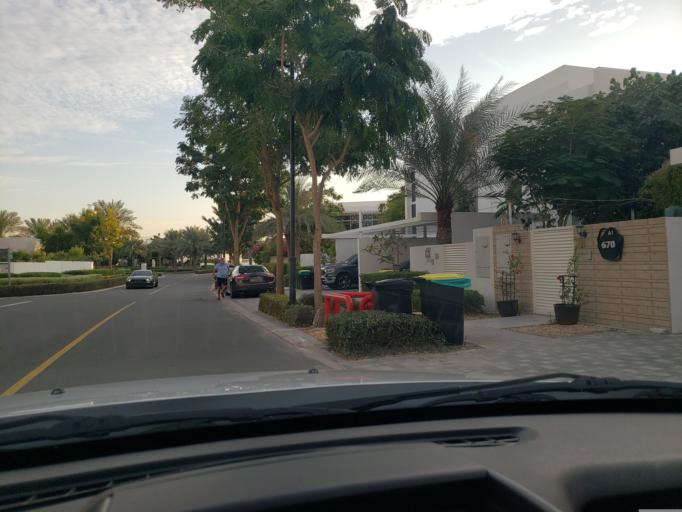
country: AE
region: Dubai
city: Dubai
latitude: 25.0180
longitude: 55.2709
